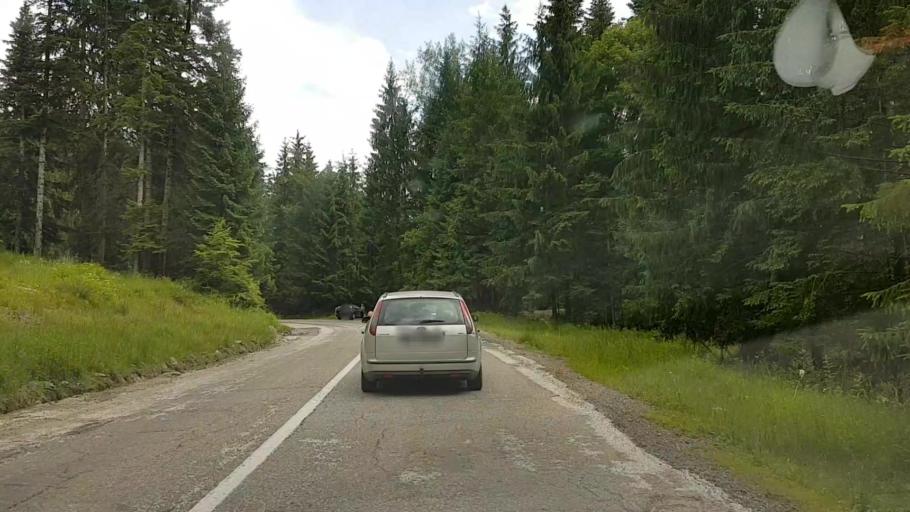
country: RO
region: Neamt
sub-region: Comuna Pangarati
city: Pangarati
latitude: 46.9719
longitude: 26.1171
